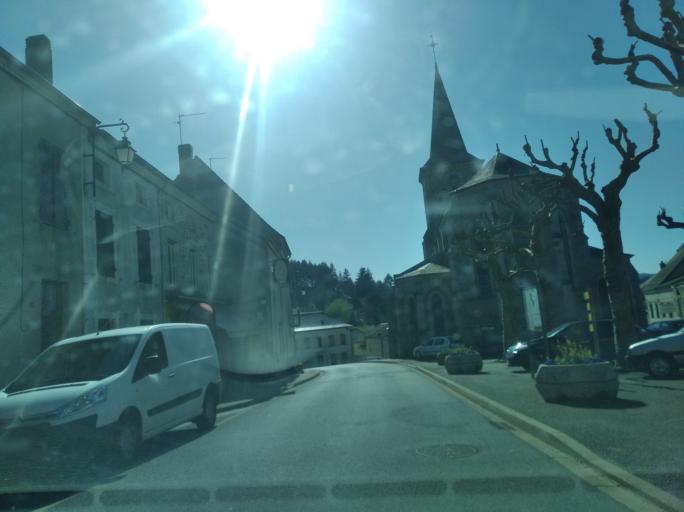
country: FR
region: Auvergne
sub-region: Departement de l'Allier
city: Le Mayet-de-Montagne
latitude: 46.0729
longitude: 3.6684
